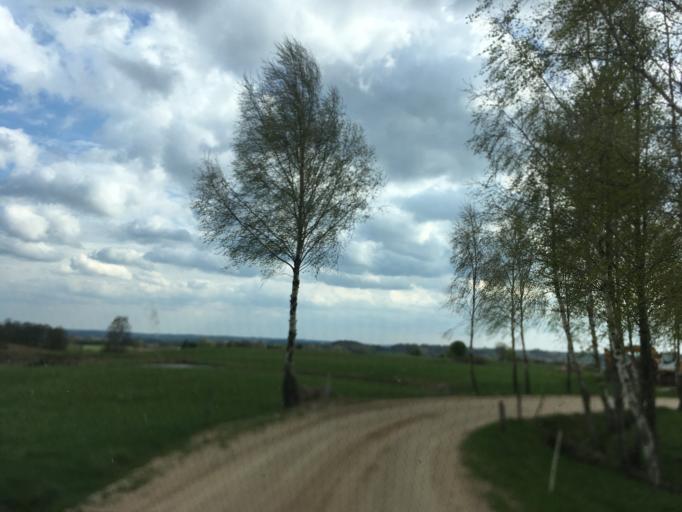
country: PL
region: Podlasie
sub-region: Powiat sejnenski
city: Punsk
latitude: 54.3845
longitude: 22.9721
